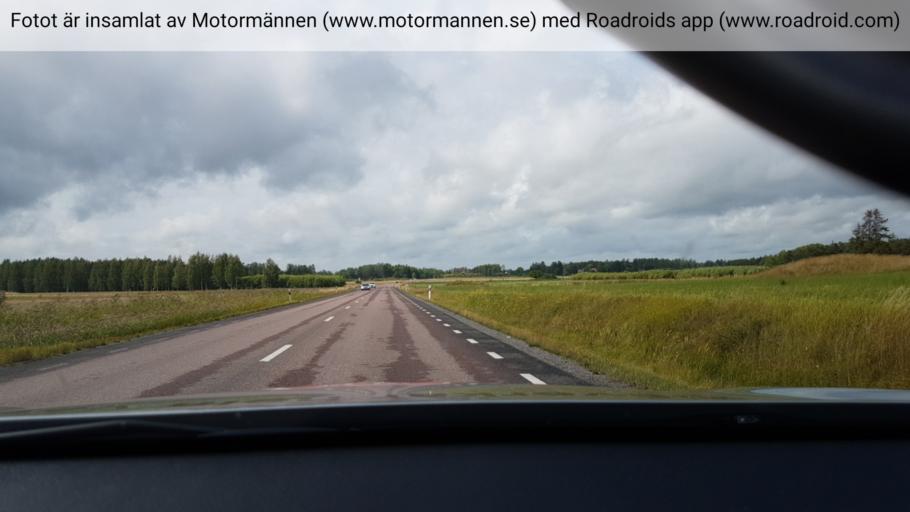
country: SE
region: Uppsala
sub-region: Osthammars Kommun
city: Bjorklinge
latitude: 59.9339
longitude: 17.4750
